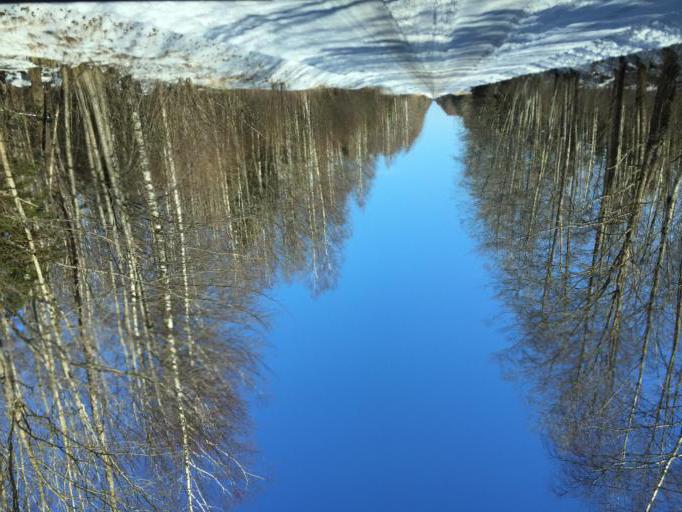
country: LV
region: Salacgrivas
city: Ainazi
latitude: 58.0282
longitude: 24.5504
